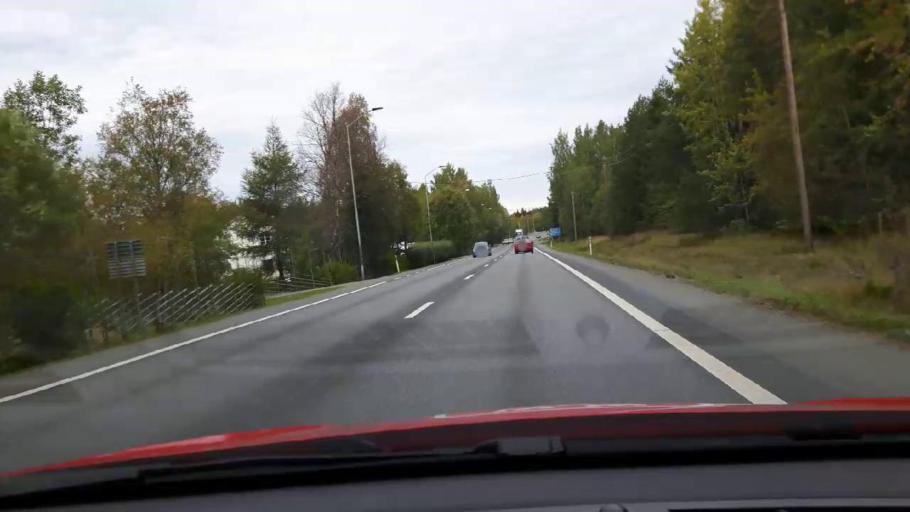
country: SE
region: Jaemtland
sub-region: OEstersunds Kommun
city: Brunflo
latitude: 63.1020
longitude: 14.7961
